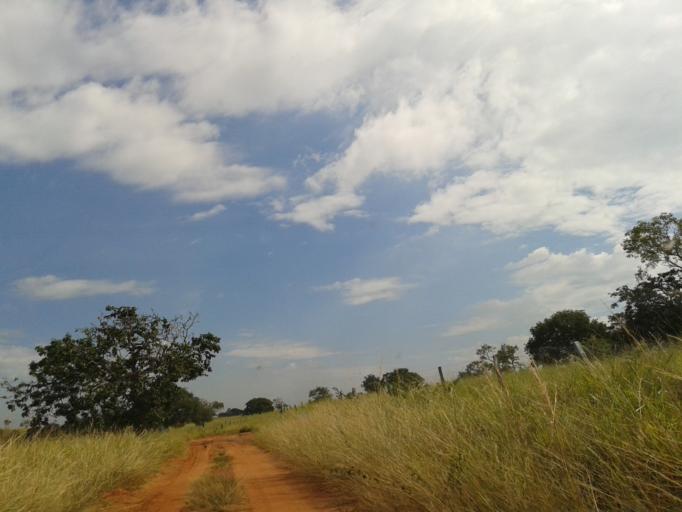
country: BR
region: Minas Gerais
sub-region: Campina Verde
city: Campina Verde
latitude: -19.3928
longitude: -49.6394
